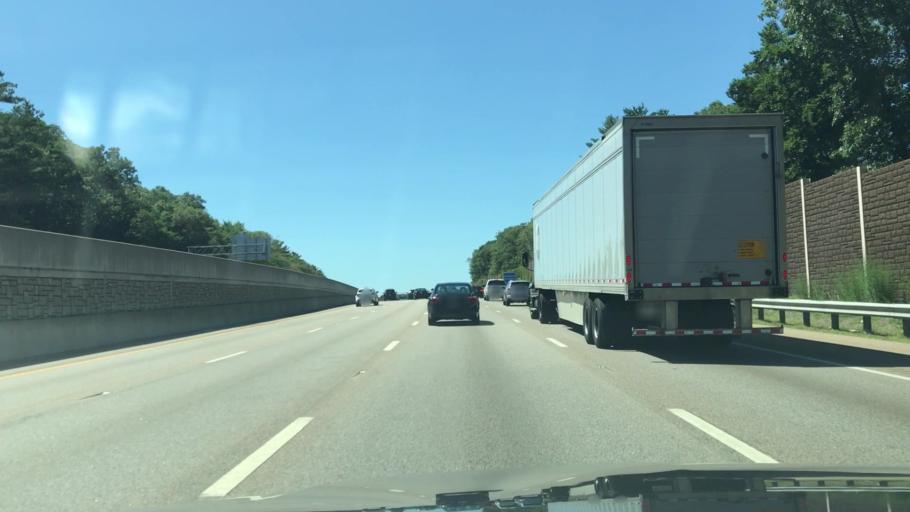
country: US
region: Massachusetts
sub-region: Norfolk County
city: Dedham
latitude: 42.2200
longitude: -71.1619
